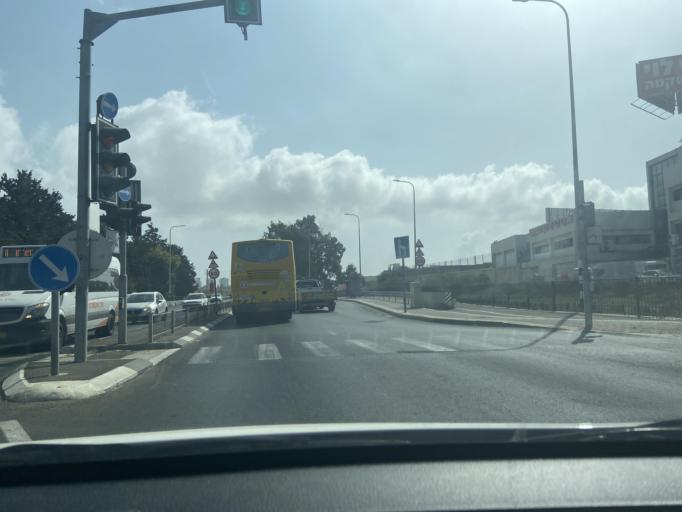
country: IL
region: Northern District
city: Nahariya
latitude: 33.0334
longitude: 35.1043
